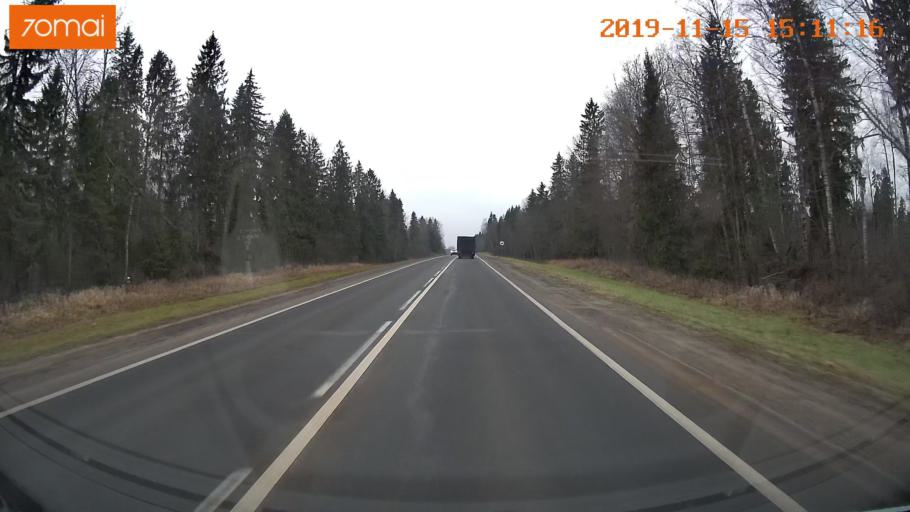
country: RU
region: Jaroslavl
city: Prechistoye
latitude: 58.3385
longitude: 40.2436
